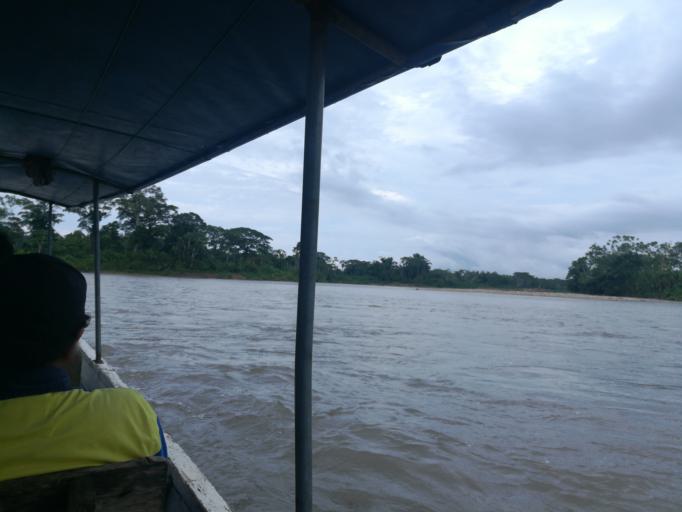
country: EC
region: Orellana
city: Boca Suno
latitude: -0.7548
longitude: -77.1543
